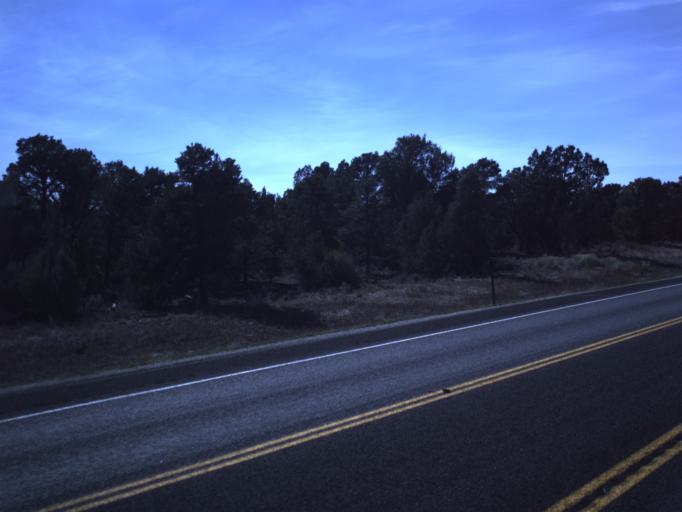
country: US
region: Colorado
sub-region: Dolores County
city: Dove Creek
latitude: 37.8233
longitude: -109.0655
